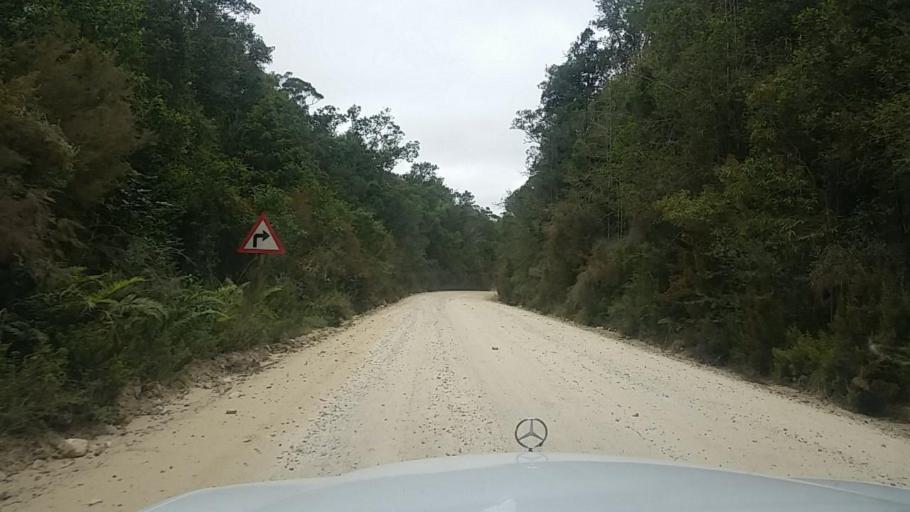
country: ZA
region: Western Cape
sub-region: Eden District Municipality
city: Knysna
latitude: -33.9726
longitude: 23.1464
